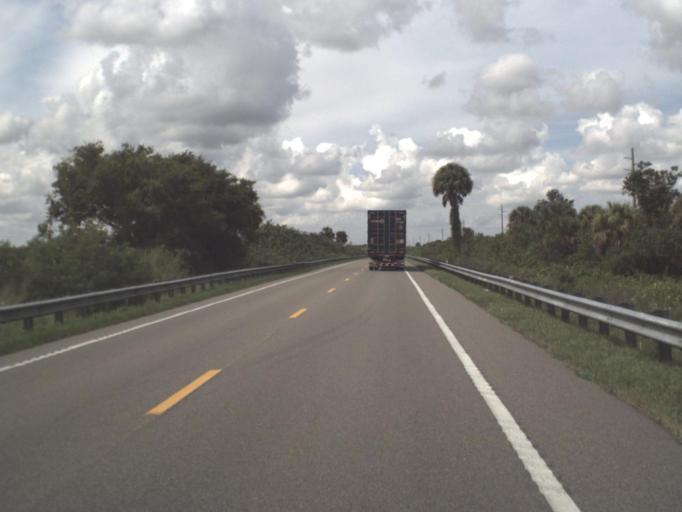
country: US
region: Florida
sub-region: Highlands County
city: Lake Placid
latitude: 27.2097
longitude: -81.1586
